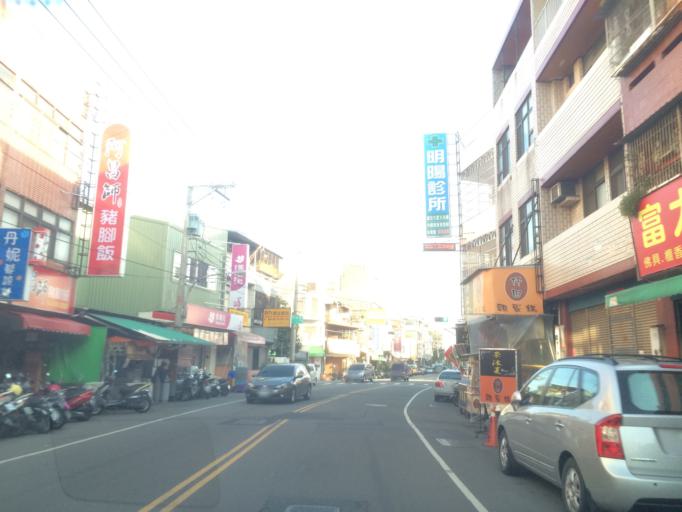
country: TW
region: Taiwan
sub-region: Taichung City
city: Taichung
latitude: 24.1919
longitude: 120.6828
